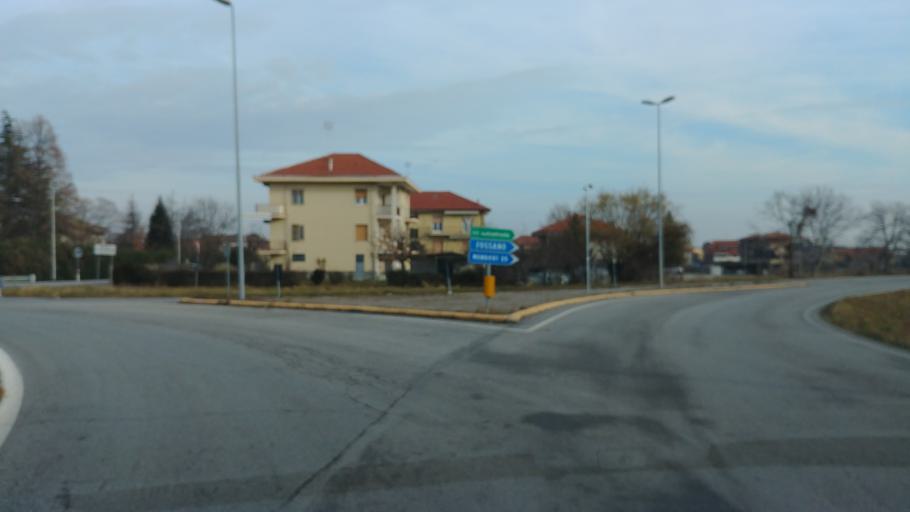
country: IT
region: Piedmont
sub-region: Provincia di Cuneo
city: Cuneo
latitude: 44.3826
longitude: 7.5611
